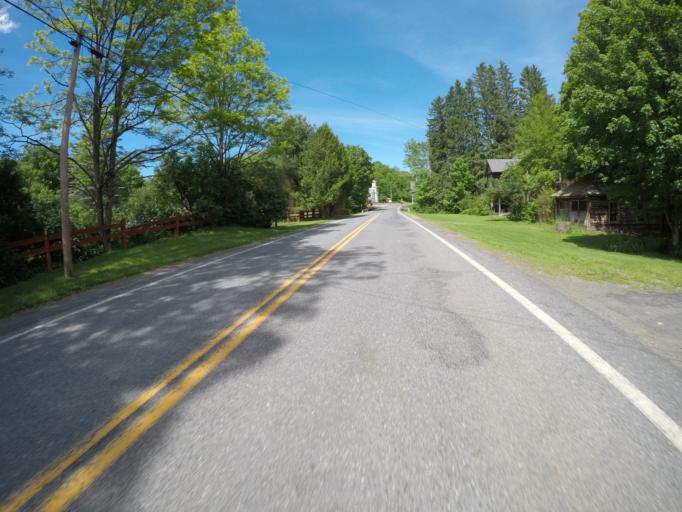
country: US
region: New York
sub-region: Delaware County
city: Delhi
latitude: 42.1226
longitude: -74.8177
